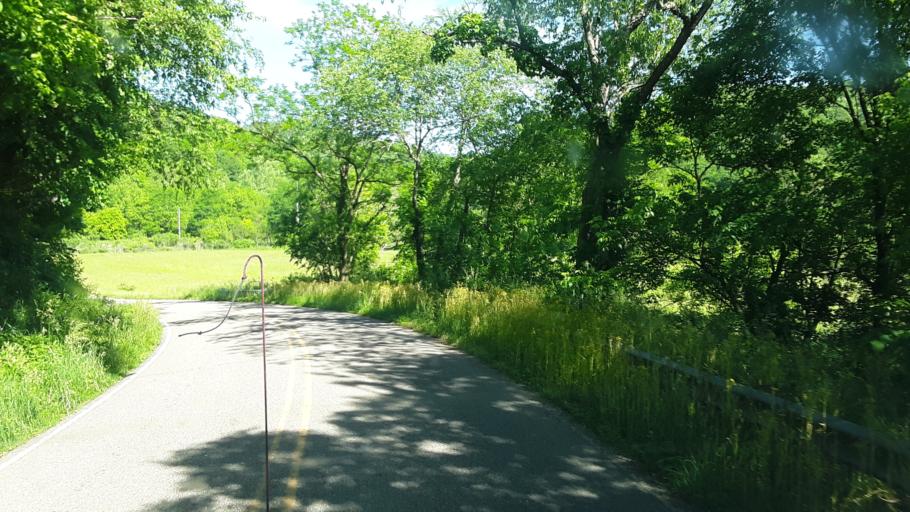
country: US
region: Ohio
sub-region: Tuscarawas County
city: Newcomerstown
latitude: 40.1789
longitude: -81.5587
